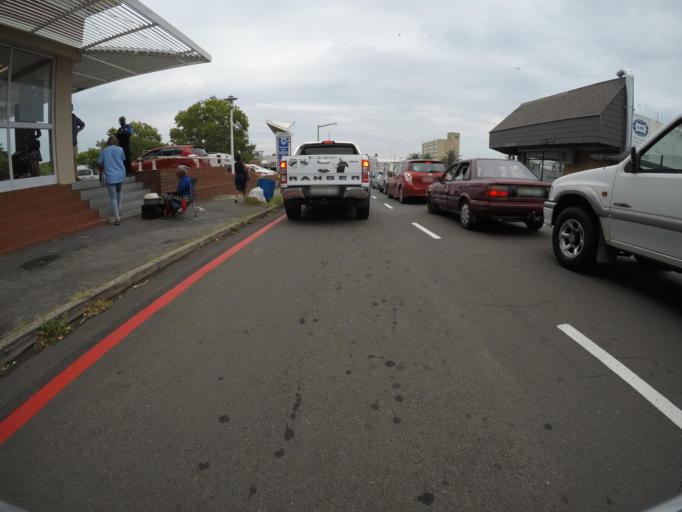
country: ZA
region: Eastern Cape
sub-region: Buffalo City Metropolitan Municipality
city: East London
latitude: -32.9827
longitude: 27.9017
